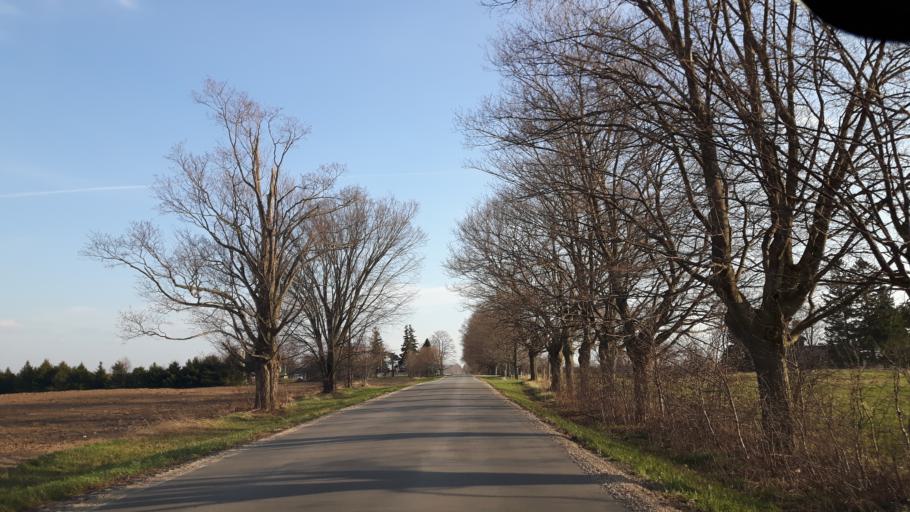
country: CA
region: Ontario
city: Goderich
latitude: 43.6412
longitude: -81.6643
